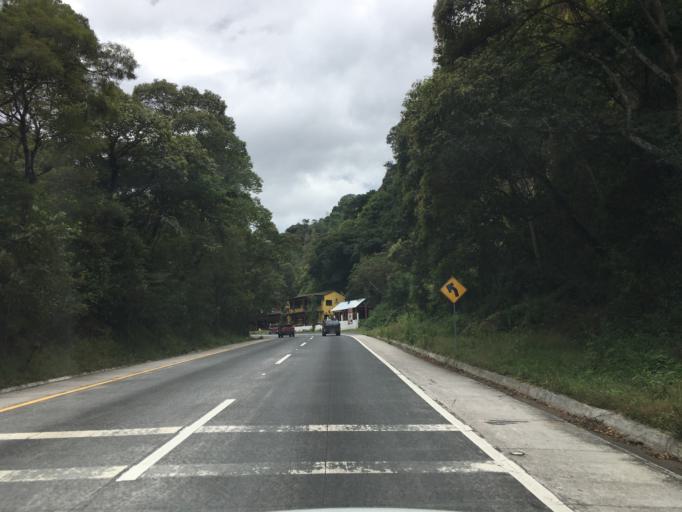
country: GT
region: Sacatepequez
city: Santa Lucia Milpas Altas
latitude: 14.5601
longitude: -90.6923
